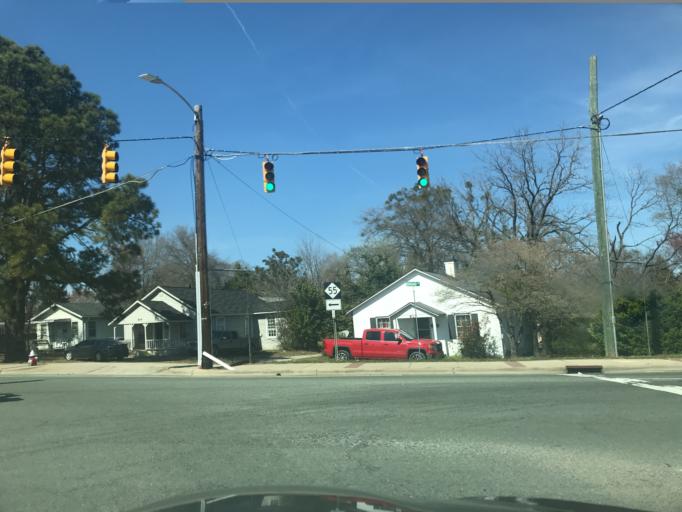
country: US
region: North Carolina
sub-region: Wake County
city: Fuquay-Varina
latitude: 35.5924
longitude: -78.7930
